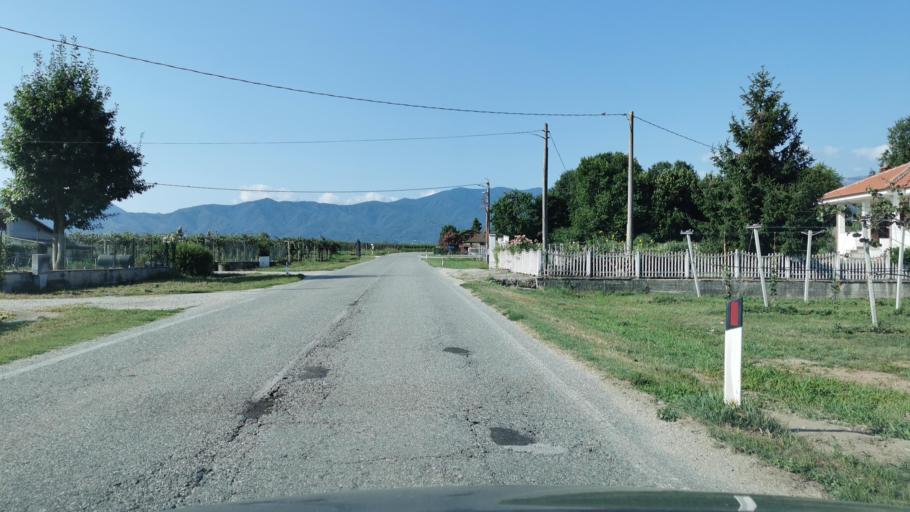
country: IT
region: Piedmont
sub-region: Provincia di Cuneo
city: Revello
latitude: 44.6809
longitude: 7.4117
